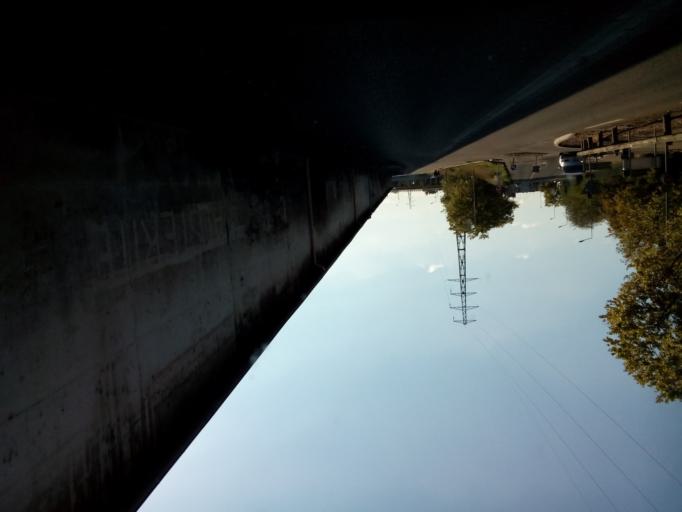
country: FR
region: Rhone-Alpes
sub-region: Departement du Rhone
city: Venissieux
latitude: 45.7052
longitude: 4.8965
